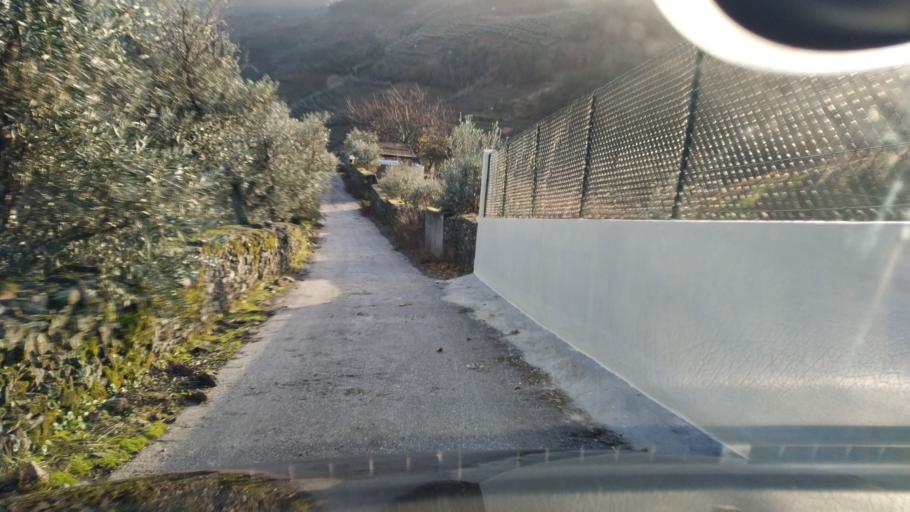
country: PT
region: Vila Real
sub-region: Vila Real
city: Vila Real
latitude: 41.2557
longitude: -7.7568
